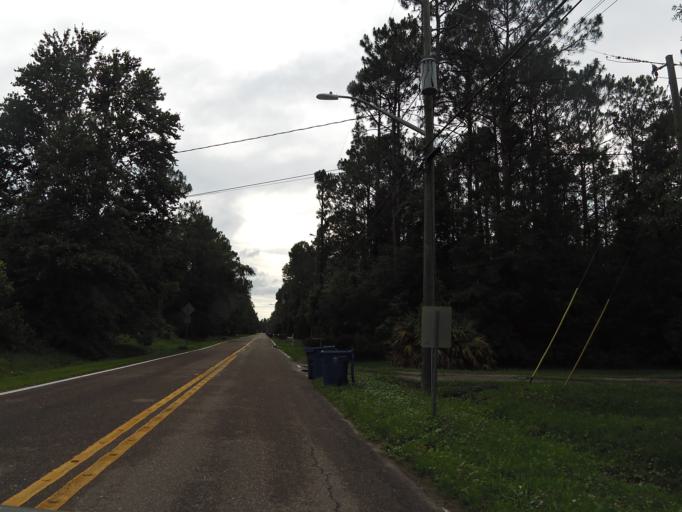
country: US
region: Florida
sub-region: Nassau County
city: Nassau Village-Ratliff
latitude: 30.5501
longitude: -81.6965
